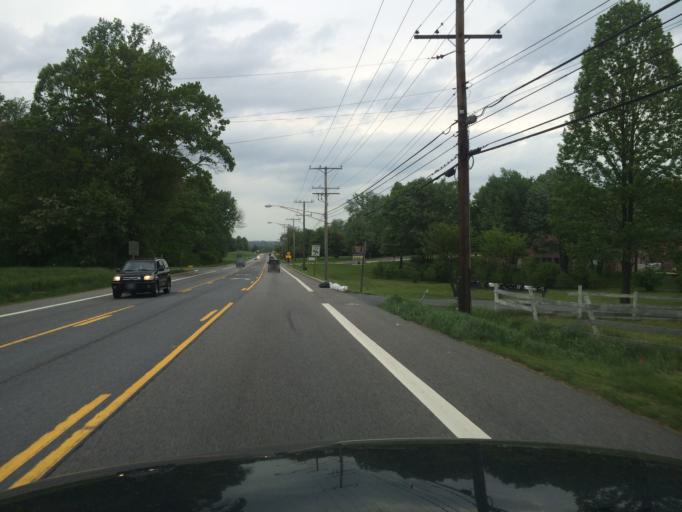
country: US
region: Maryland
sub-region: Carroll County
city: Sykesville
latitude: 39.3314
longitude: -76.9496
